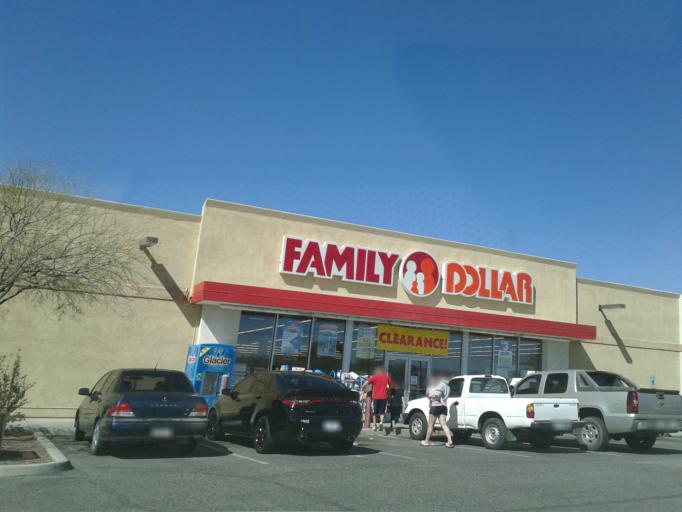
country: US
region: Arizona
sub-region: Pima County
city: Marana
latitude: 32.4525
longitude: -111.2177
